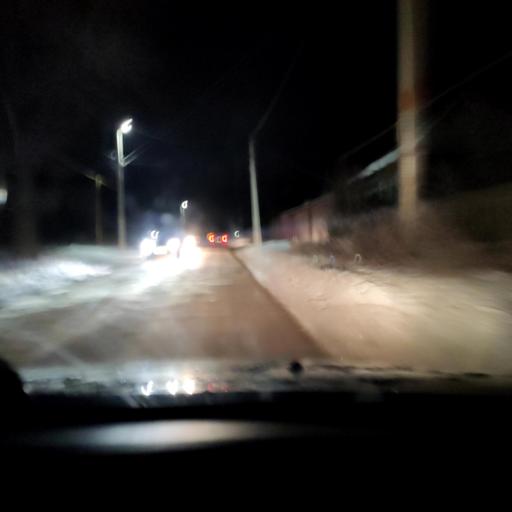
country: RU
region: Samara
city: Novyy Buyan
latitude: 53.6799
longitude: 50.0377
